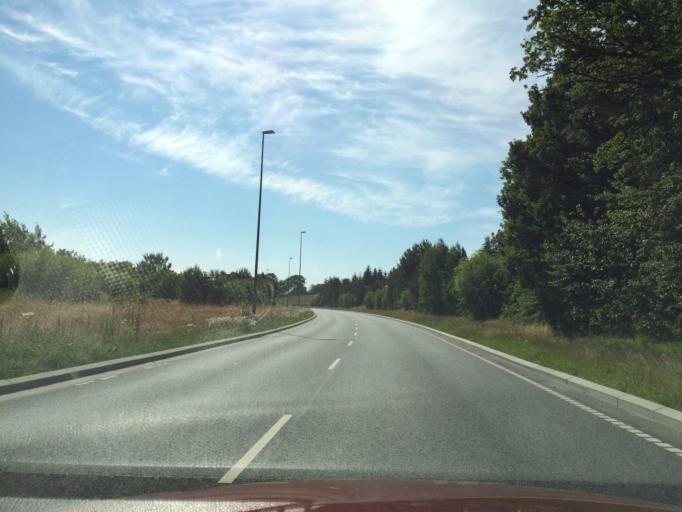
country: DK
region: Central Jutland
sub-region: Silkeborg Kommune
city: Silkeborg
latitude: 56.1969
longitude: 9.5314
